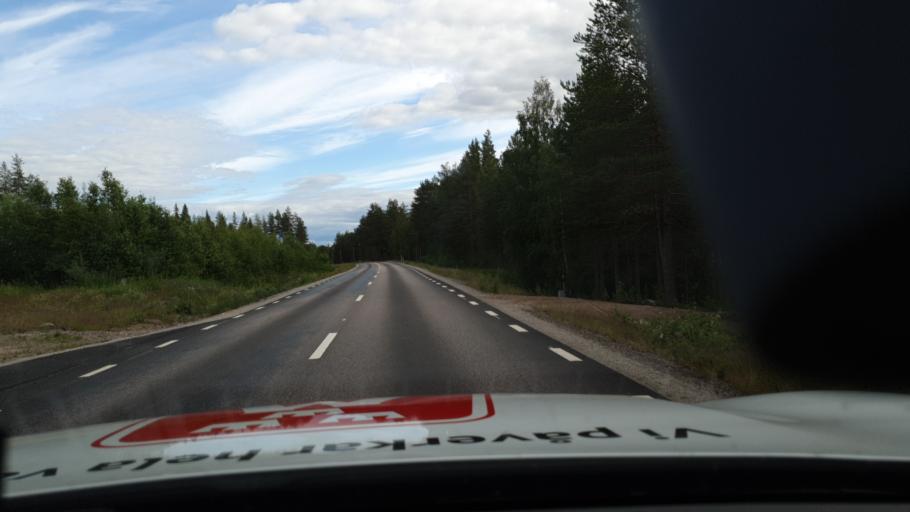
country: SE
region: Norrbotten
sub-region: Overkalix Kommun
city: OEverkalix
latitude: 66.3921
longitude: 22.8195
